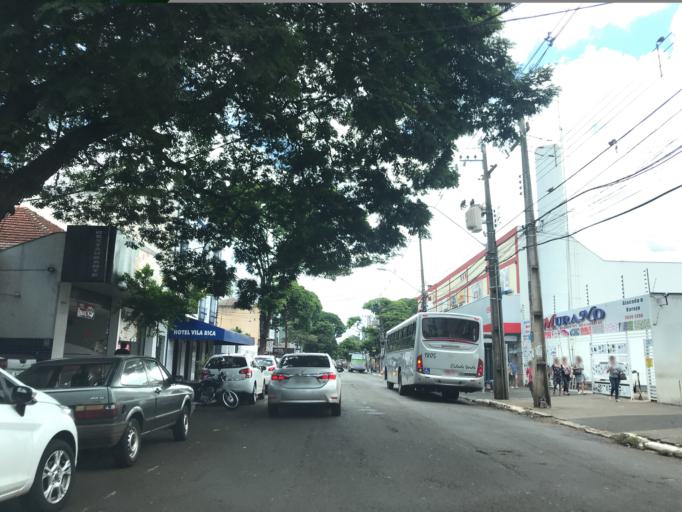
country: BR
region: Parana
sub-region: Maringa
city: Maringa
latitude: -23.4198
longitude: -51.9360
